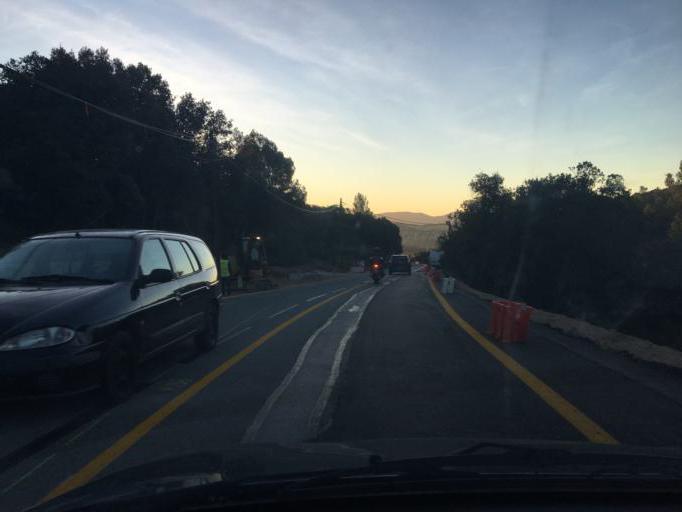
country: FR
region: Provence-Alpes-Cote d'Azur
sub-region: Departement du Var
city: Taradeau
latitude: 43.4596
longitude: 6.4188
